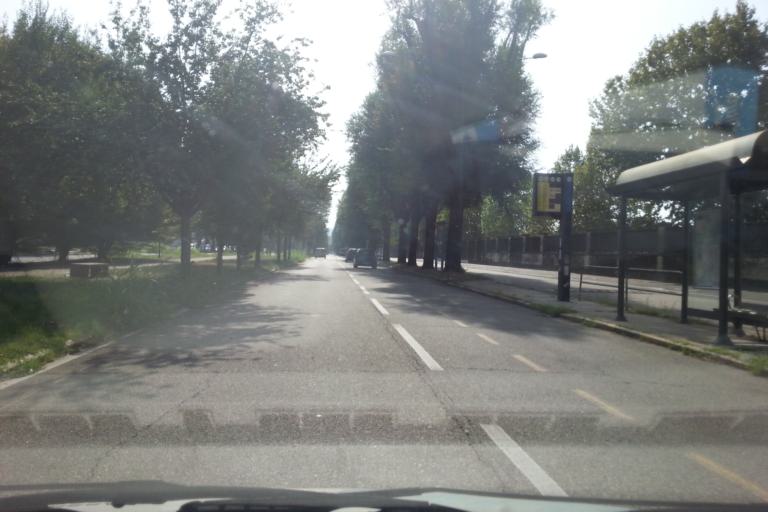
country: IT
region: Piedmont
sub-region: Provincia di Torino
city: Gerbido
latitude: 45.0329
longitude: 7.6327
